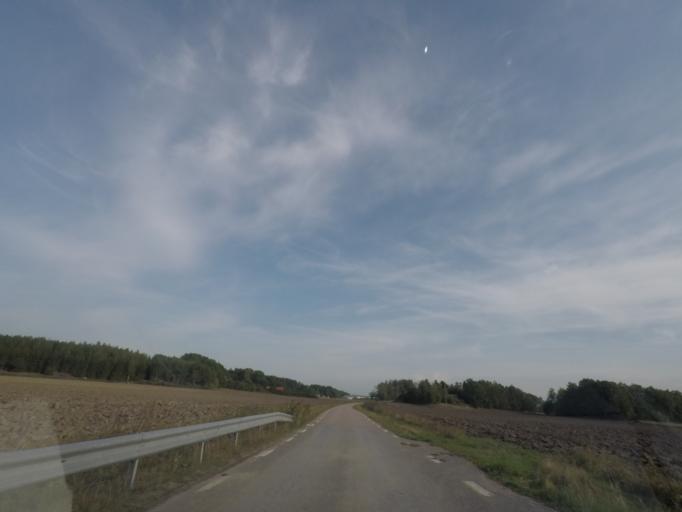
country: SE
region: Vaestmanland
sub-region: Kungsors Kommun
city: Kungsoer
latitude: 59.4908
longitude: 16.1602
